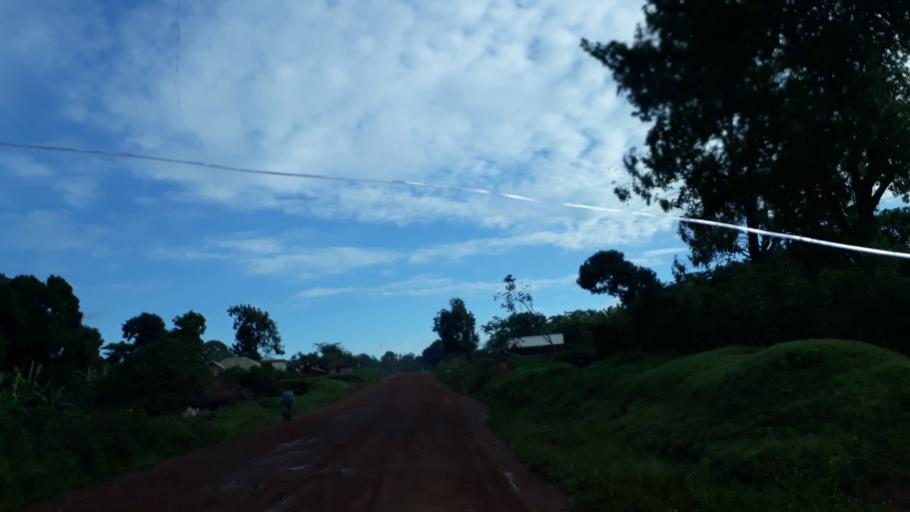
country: UG
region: Northern Region
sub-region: Zombo District
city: Paidha
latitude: 2.2390
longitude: 30.8611
